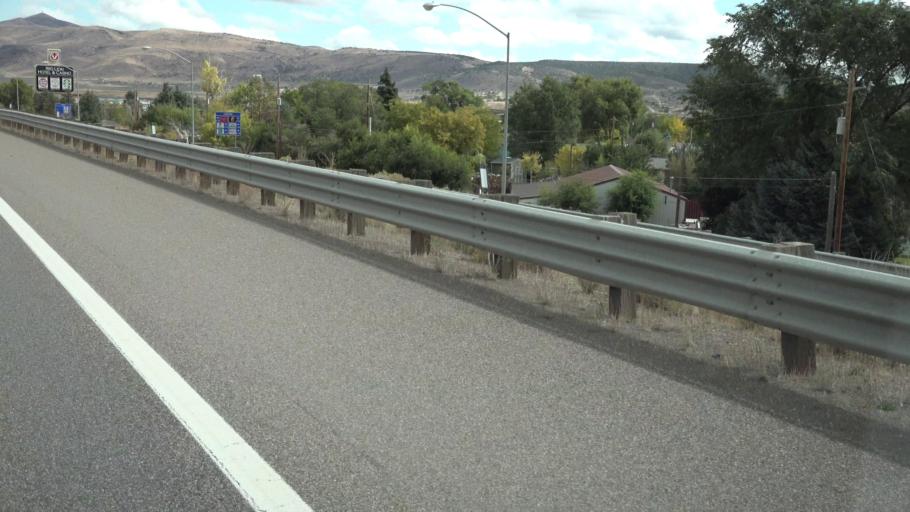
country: US
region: Nevada
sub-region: Elko County
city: Elko
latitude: 40.8501
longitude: -115.7510
